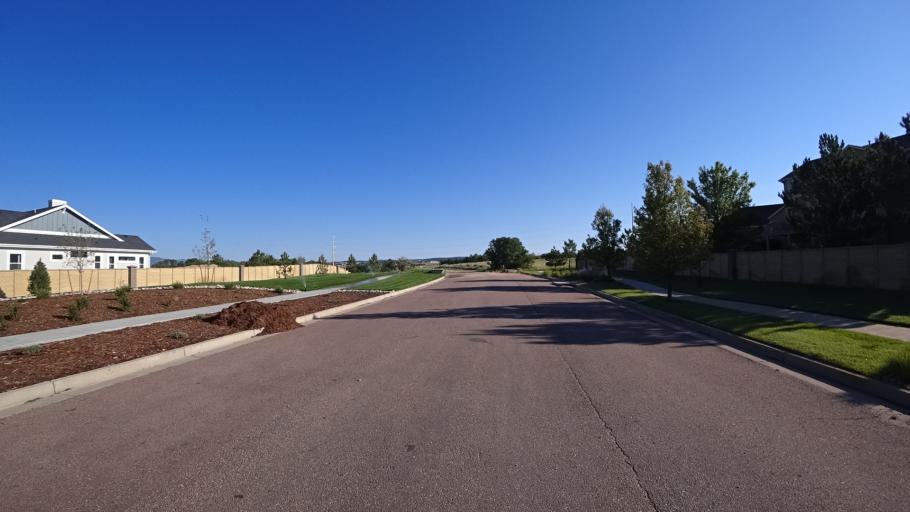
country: US
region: Colorado
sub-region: El Paso County
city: Gleneagle
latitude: 38.9867
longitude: -104.7739
